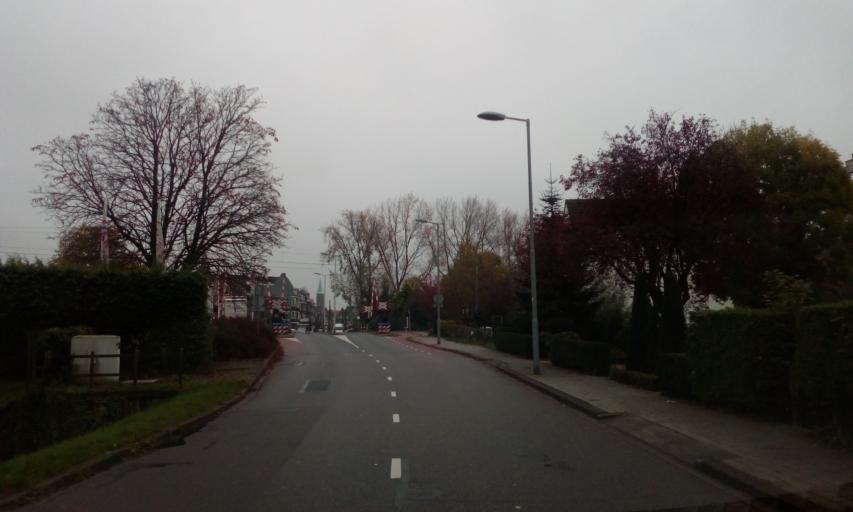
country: NL
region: South Holland
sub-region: Gemeente Rotterdam
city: Rotterdam
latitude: 51.9458
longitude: 4.4652
